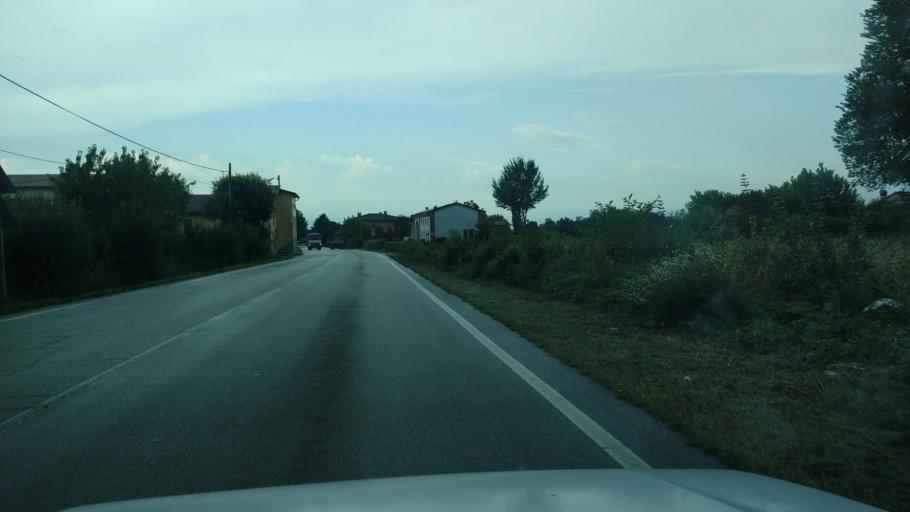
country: IT
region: Veneto
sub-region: Provincia di Vicenza
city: Schiavon
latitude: 45.7079
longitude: 11.6482
